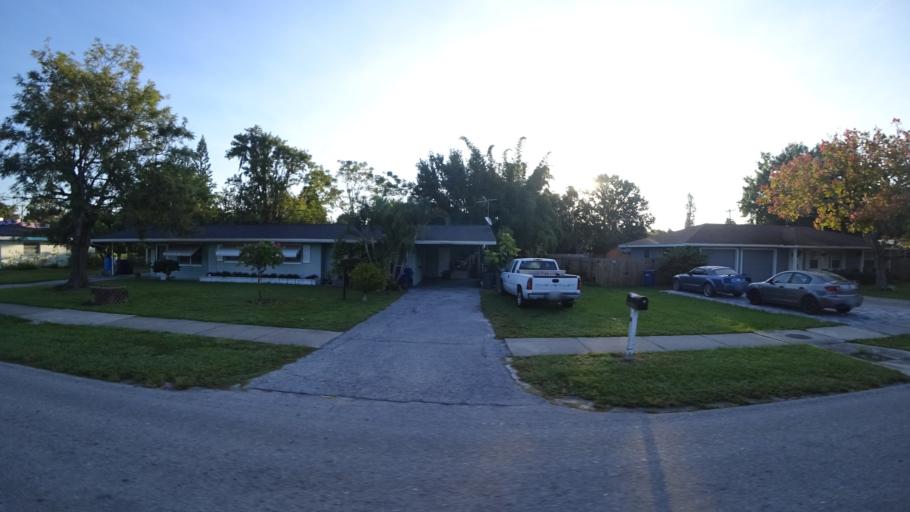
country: US
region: Florida
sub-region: Manatee County
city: South Bradenton
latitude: 27.4599
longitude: -82.5820
